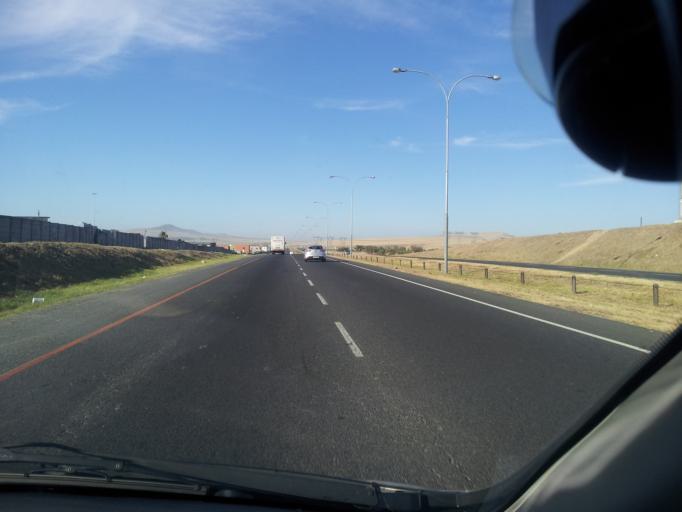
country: ZA
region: Western Cape
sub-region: City of Cape Town
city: Sunset Beach
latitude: -33.8227
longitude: 18.5424
